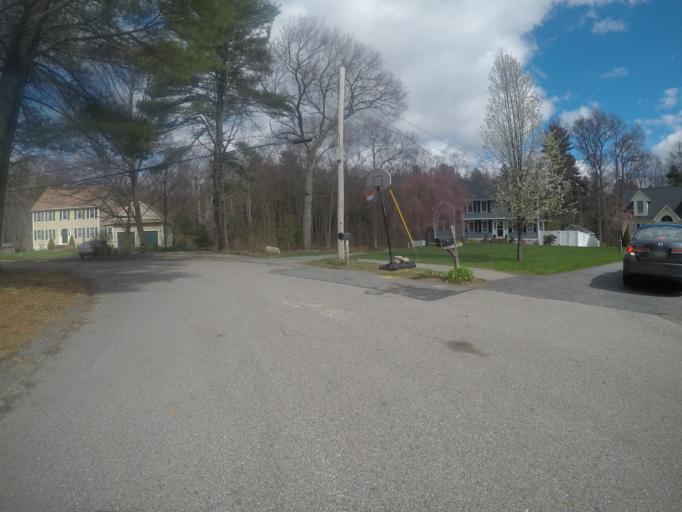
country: US
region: Massachusetts
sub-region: Bristol County
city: Easton
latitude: 42.0300
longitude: -71.1602
